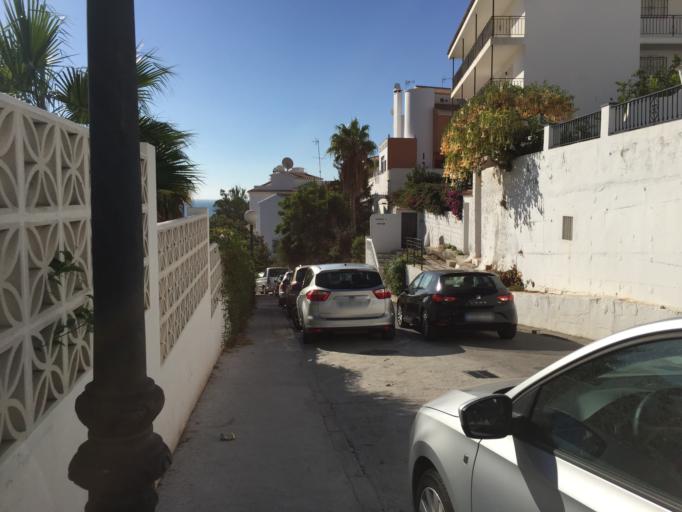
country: ES
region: Andalusia
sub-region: Provincia de Malaga
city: Nerja
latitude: 36.7516
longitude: -3.8711
